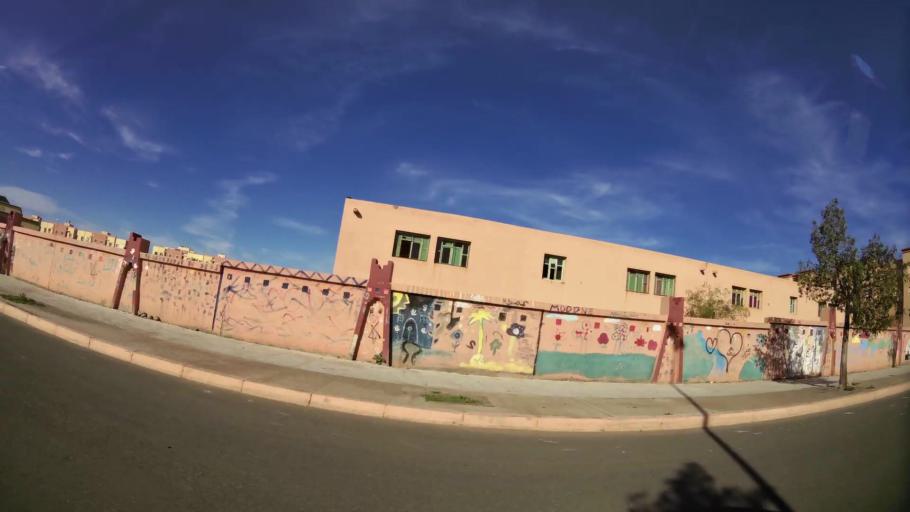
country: MA
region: Marrakech-Tensift-Al Haouz
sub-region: Marrakech
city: Marrakesh
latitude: 31.6869
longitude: -8.0721
